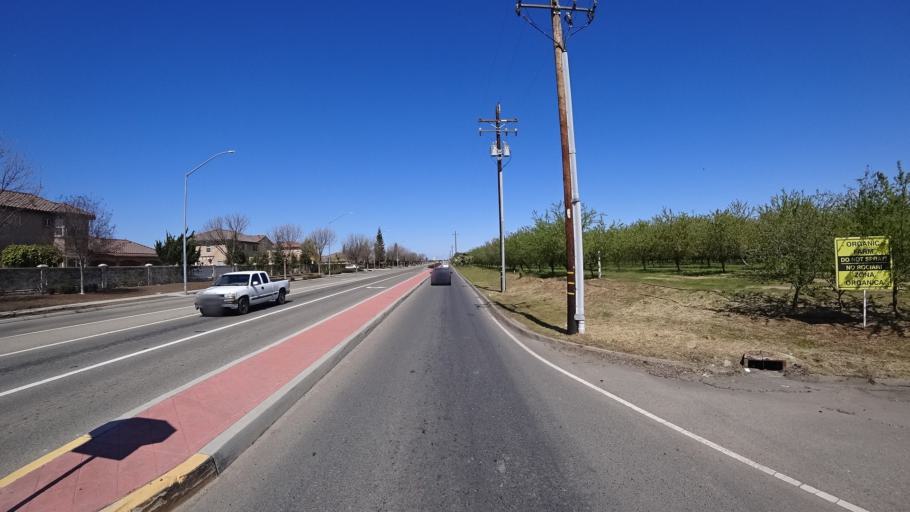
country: US
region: California
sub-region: Fresno County
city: West Park
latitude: 36.7286
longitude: -119.8444
